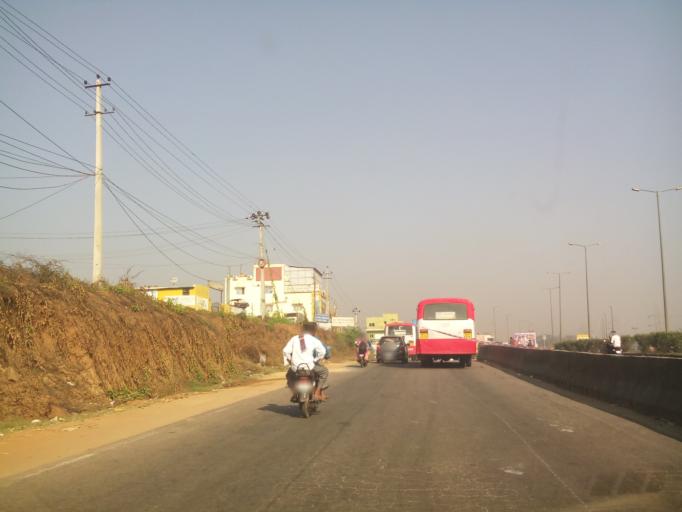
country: IN
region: Karnataka
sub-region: Bangalore Rural
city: Nelamangala
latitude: 13.0953
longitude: 77.3884
